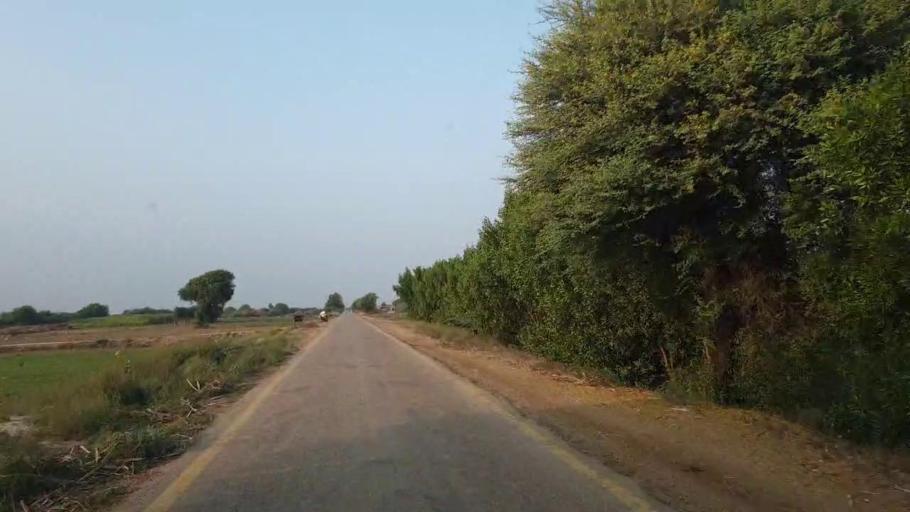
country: PK
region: Sindh
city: Tando Ghulam Ali
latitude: 25.0837
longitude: 68.9586
